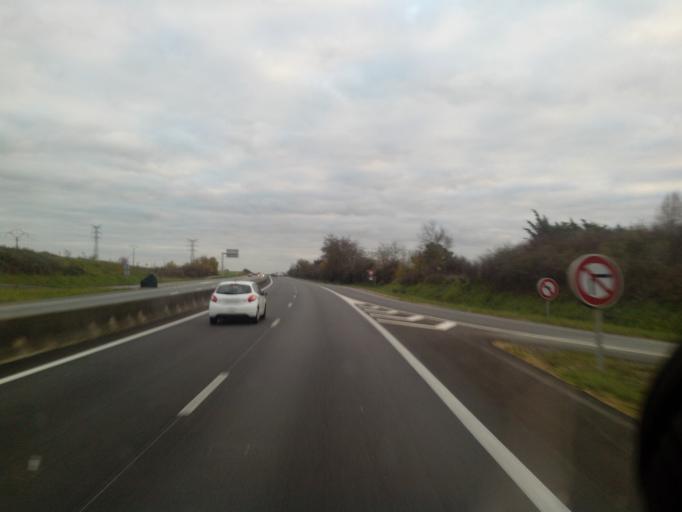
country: FR
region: Poitou-Charentes
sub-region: Departement de la Vienne
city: Montamise
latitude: 46.5970
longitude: 0.3906
